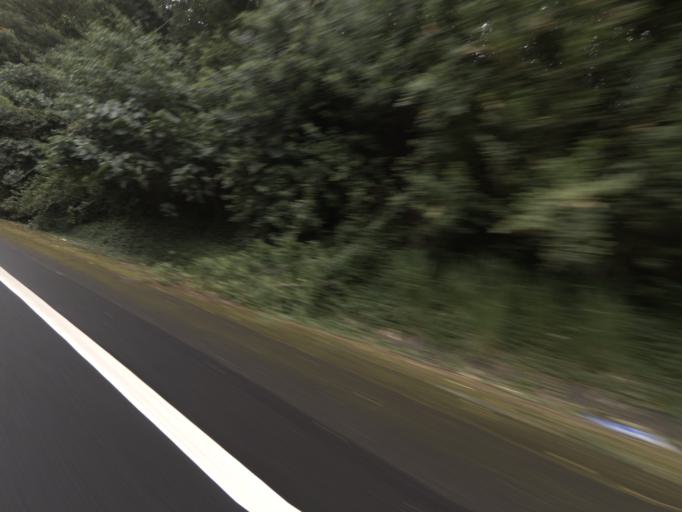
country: US
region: Hawaii
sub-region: Honolulu County
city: Kane'ohe
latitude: 21.3926
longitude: -157.8152
